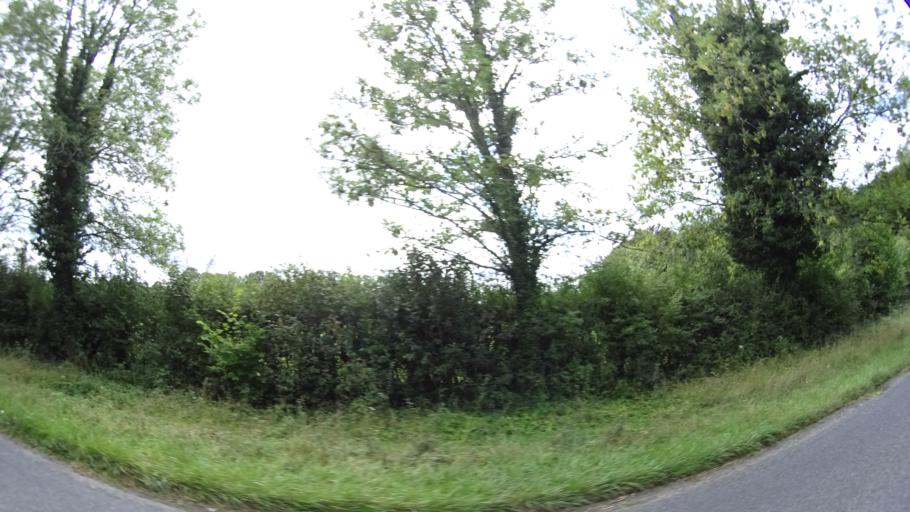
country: GB
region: England
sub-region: Wiltshire
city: Tidworth
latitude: 51.1820
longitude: -1.6507
